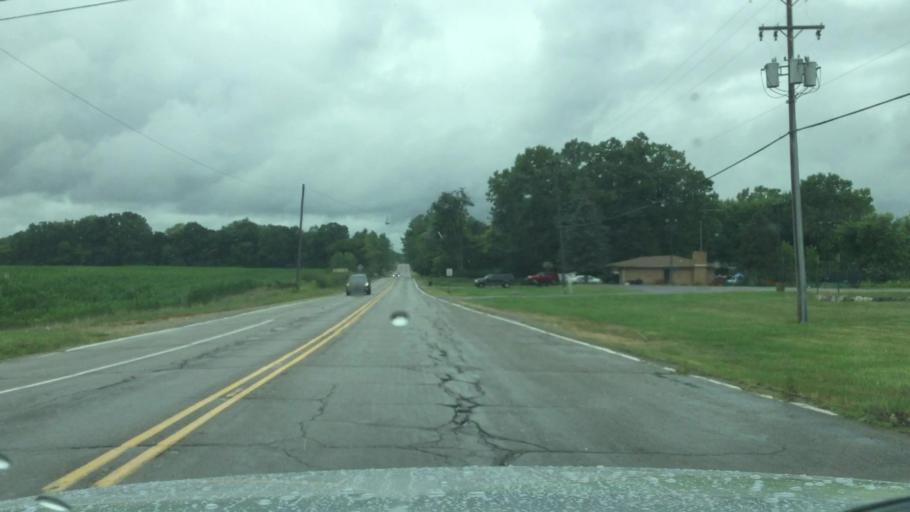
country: US
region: Michigan
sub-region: Genesee County
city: Beecher
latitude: 43.0754
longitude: -83.7537
